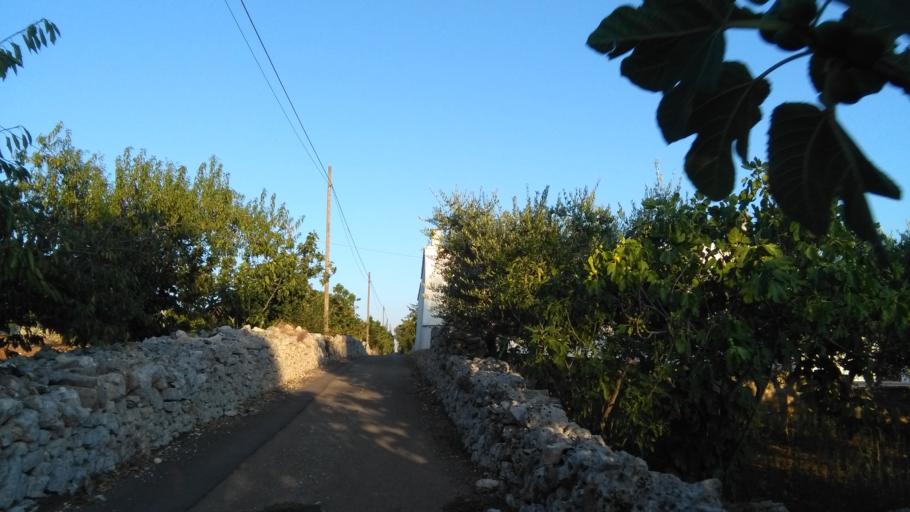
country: IT
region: Apulia
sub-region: Provincia di Bari
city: Putignano
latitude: 40.8253
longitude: 17.0953
